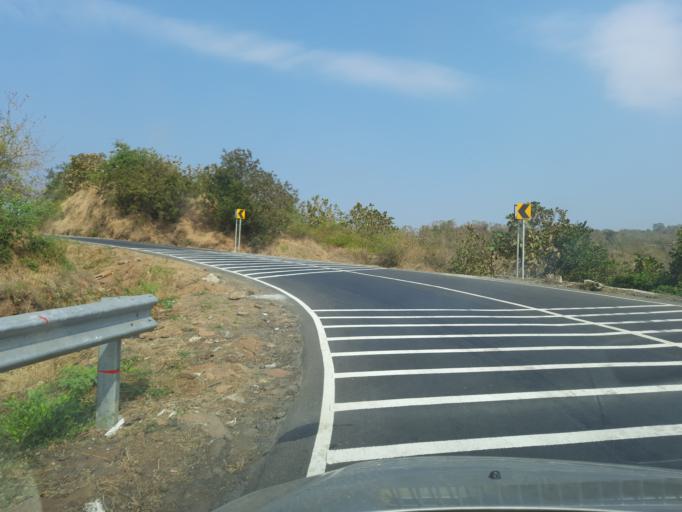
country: IN
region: Maharashtra
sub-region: Nashik Division
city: Surgana
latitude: 20.2577
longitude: 73.6114
